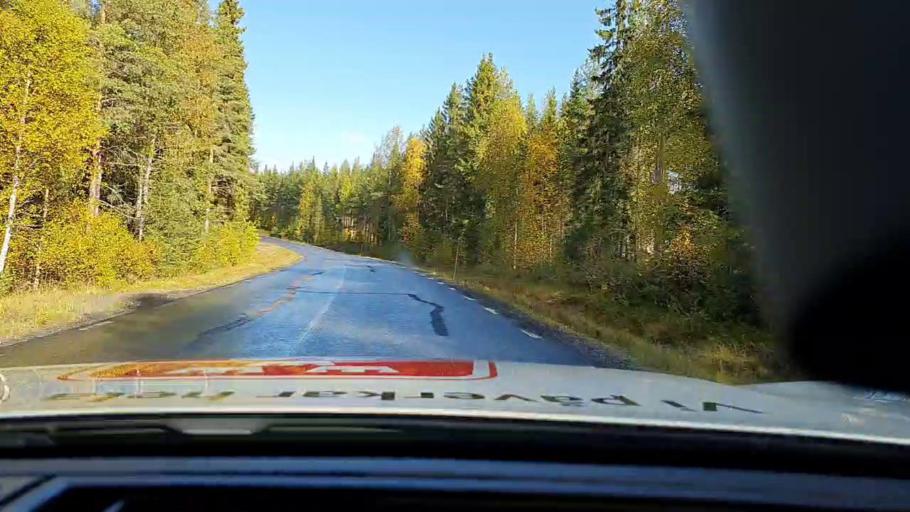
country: SE
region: Vaesterbotten
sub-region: Skelleftea Kommun
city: Langsele
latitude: 64.9614
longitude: 20.0431
